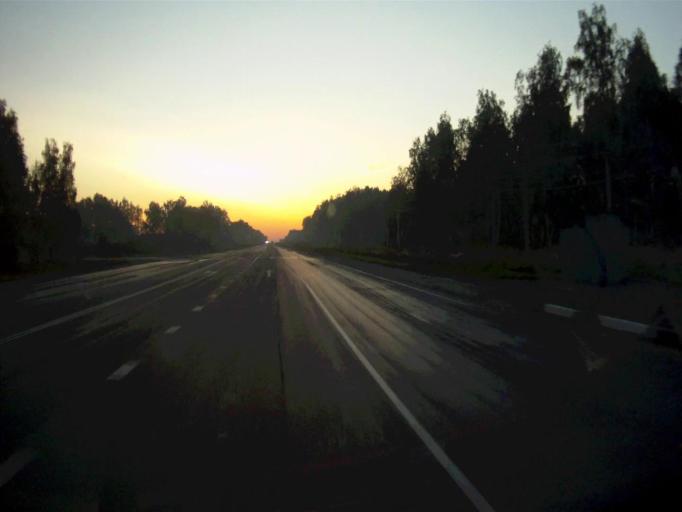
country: RU
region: Chelyabinsk
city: Poletayevo
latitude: 55.2068
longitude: 61.1031
